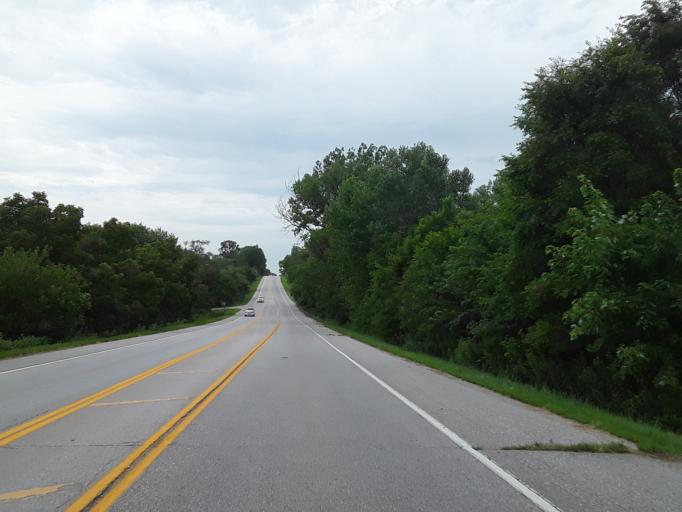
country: US
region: Nebraska
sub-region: Douglas County
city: Bennington
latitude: 41.3647
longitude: -96.0277
